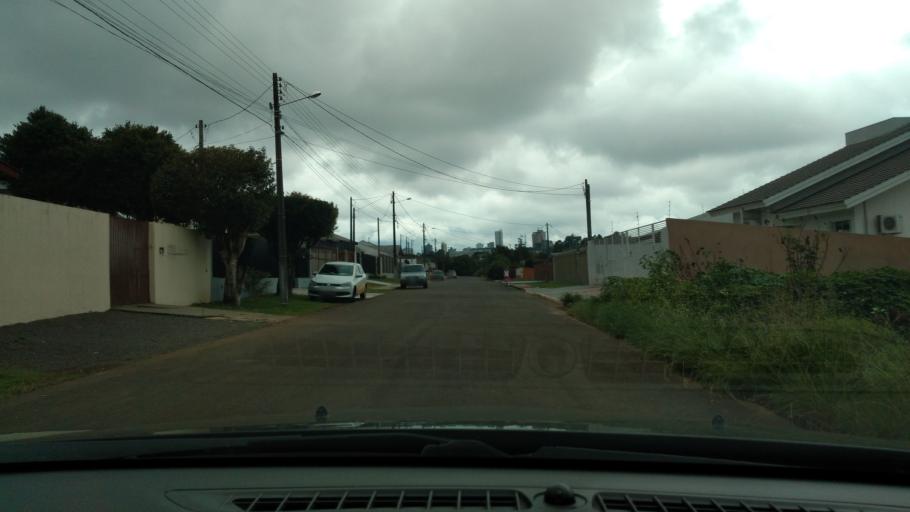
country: BR
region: Parana
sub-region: Guarapuava
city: Guarapuava
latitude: -25.3944
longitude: -51.4904
